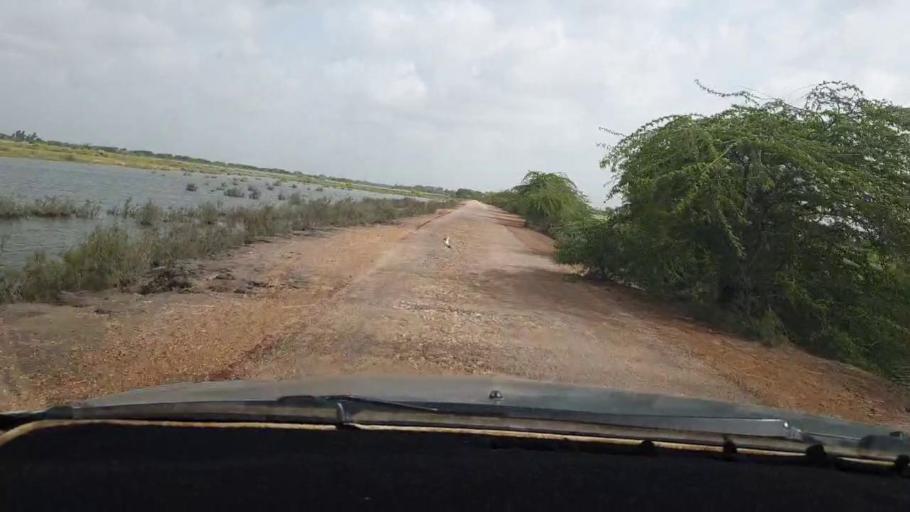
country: PK
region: Sindh
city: Tando Bago
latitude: 24.7838
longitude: 69.0275
